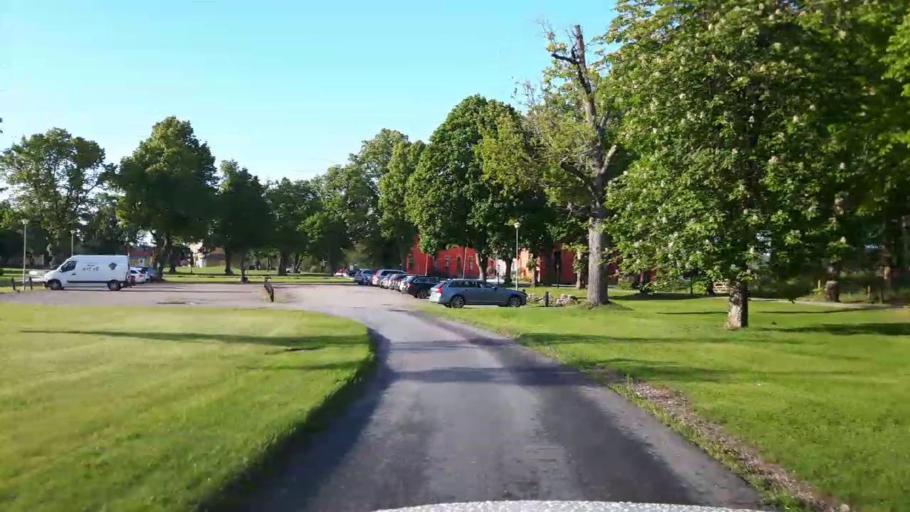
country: SE
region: Stockholm
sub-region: Upplands-Bro Kommun
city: Bro
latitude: 59.5236
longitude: 17.6732
